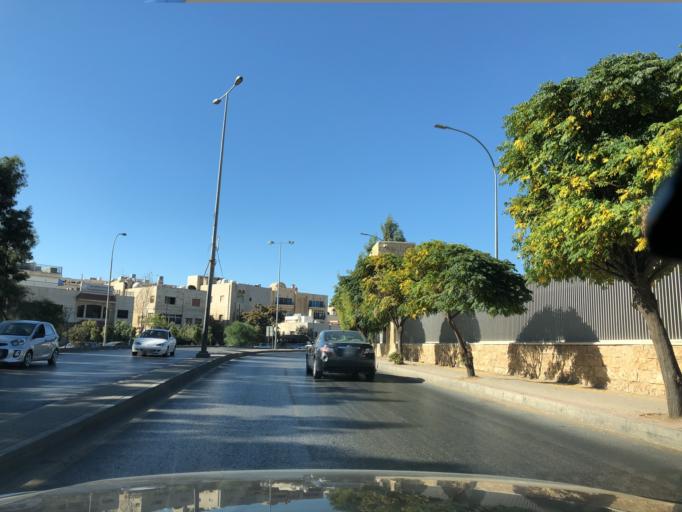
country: JO
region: Amman
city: Wadi as Sir
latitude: 31.9707
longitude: 35.8380
